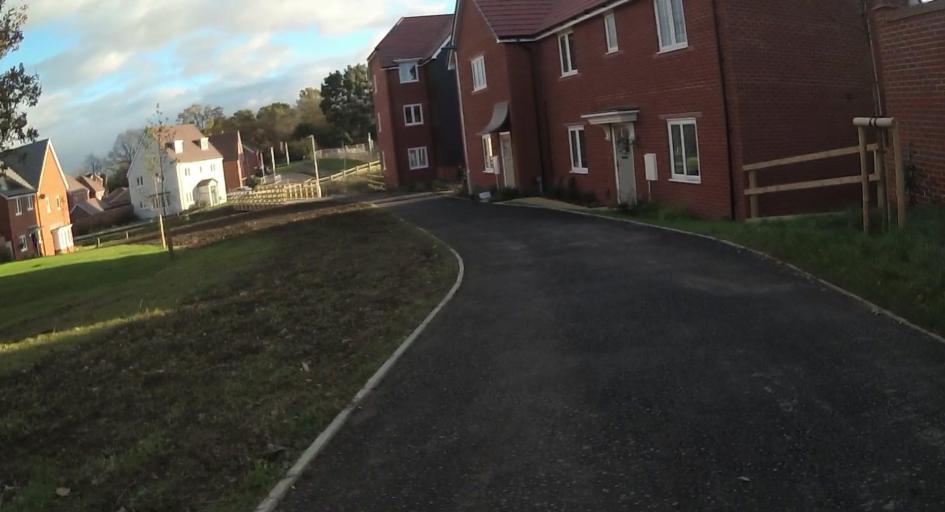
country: GB
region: England
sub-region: Bracknell Forest
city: Binfield
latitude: 51.4267
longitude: -0.7771
